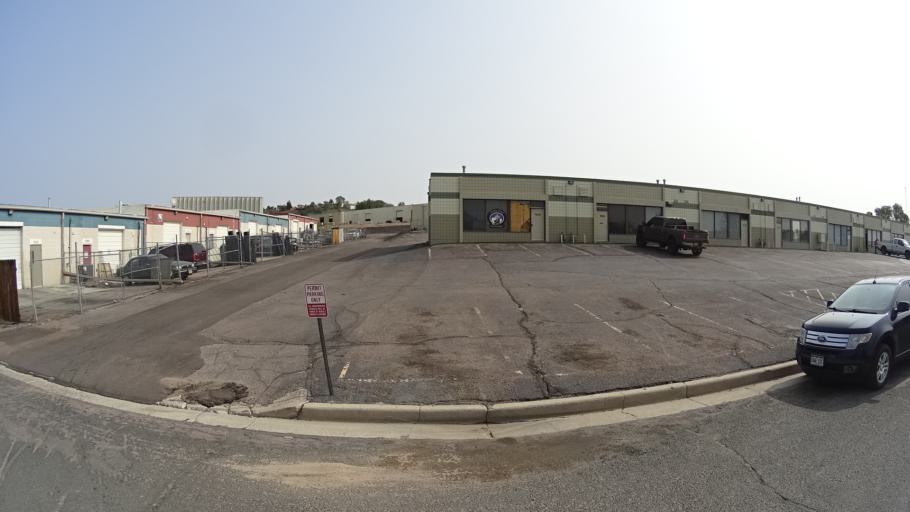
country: US
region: Colorado
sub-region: El Paso County
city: Stratmoor
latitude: 38.7939
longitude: -104.7753
